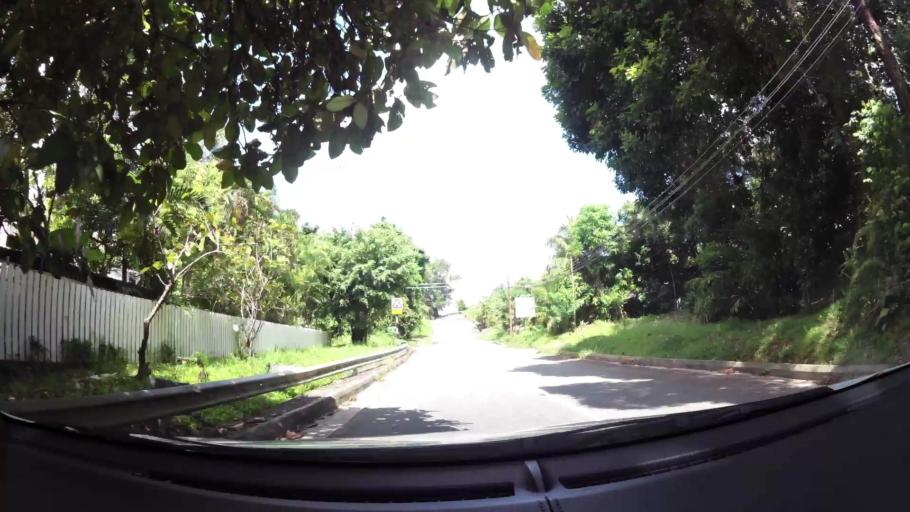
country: BN
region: Brunei and Muara
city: Bandar Seri Begawan
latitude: 4.9433
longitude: 114.9649
